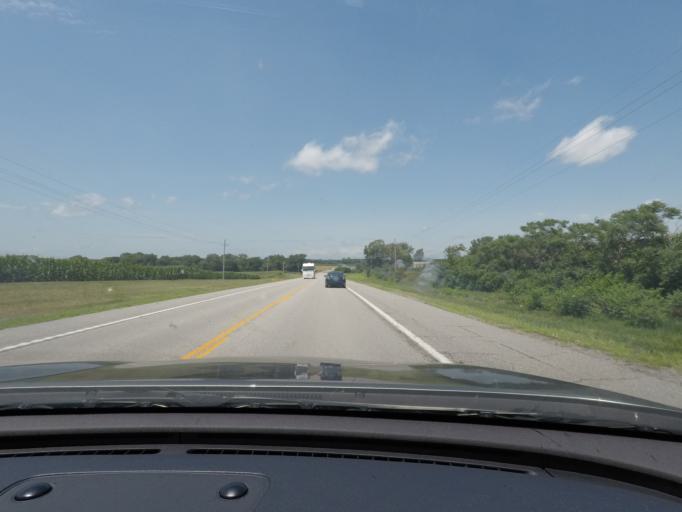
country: US
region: Missouri
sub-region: Saline County
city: Marshall
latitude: 39.1616
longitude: -93.2741
